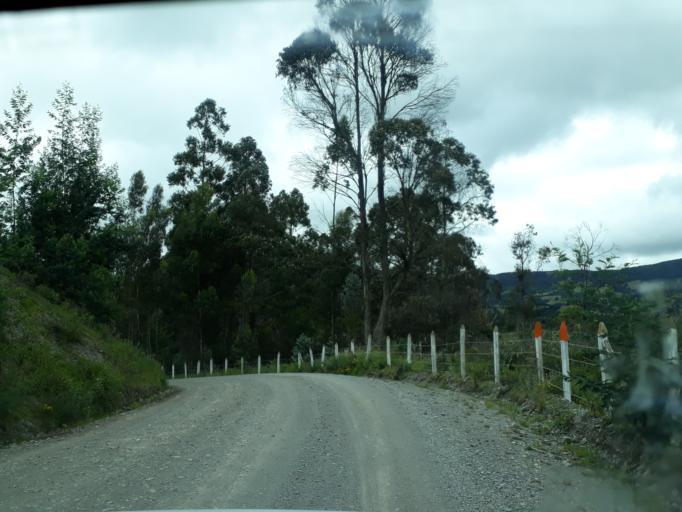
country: CO
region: Cundinamarca
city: La Mesa
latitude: 5.2878
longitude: -73.9050
